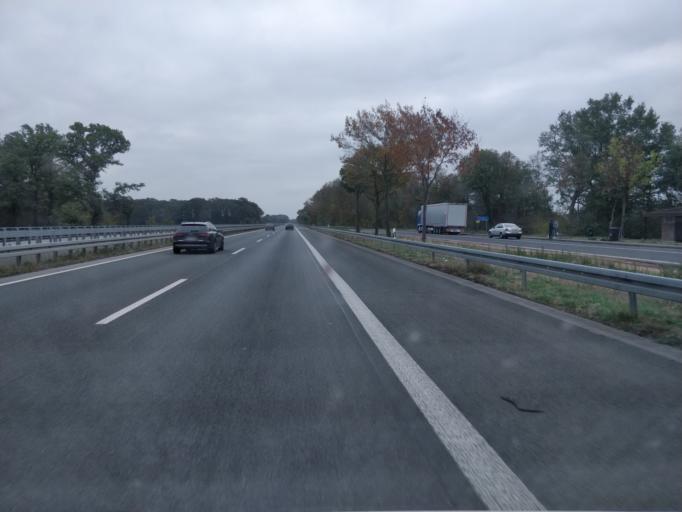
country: DE
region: North Rhine-Westphalia
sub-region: Regierungsbezirk Dusseldorf
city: Mehrhoog
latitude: 51.7787
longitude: 6.5144
